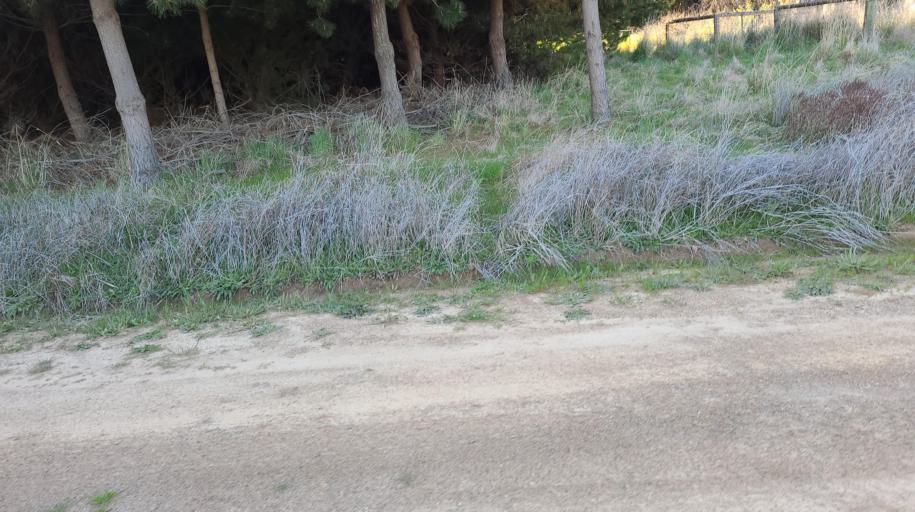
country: AU
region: New South Wales
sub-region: Blayney
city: Millthorpe
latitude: -33.4103
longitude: 149.3075
